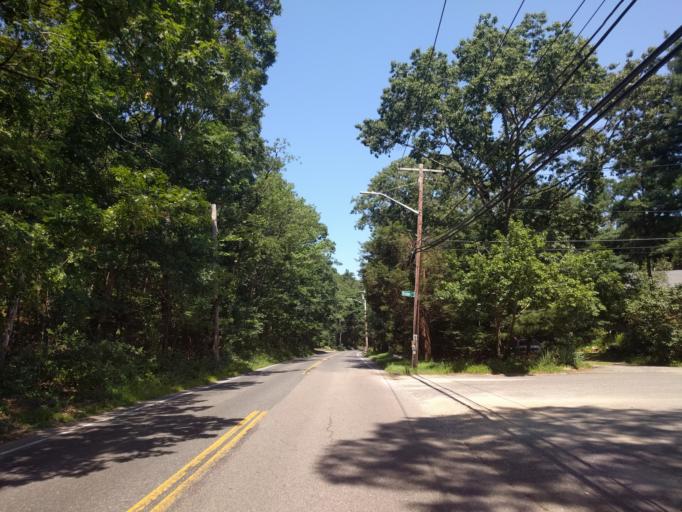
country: US
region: New York
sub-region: Suffolk County
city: Fort Salonga
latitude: 40.8857
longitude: -73.2885
